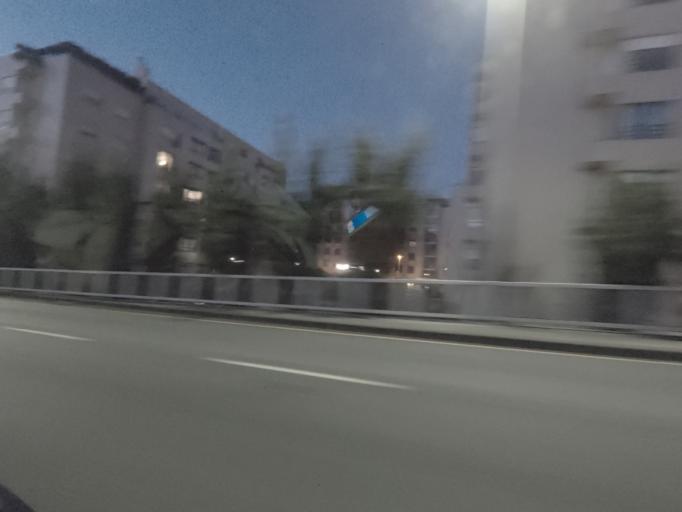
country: PT
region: Porto
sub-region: Matosinhos
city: Senhora da Hora
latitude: 41.1658
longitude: -8.6467
